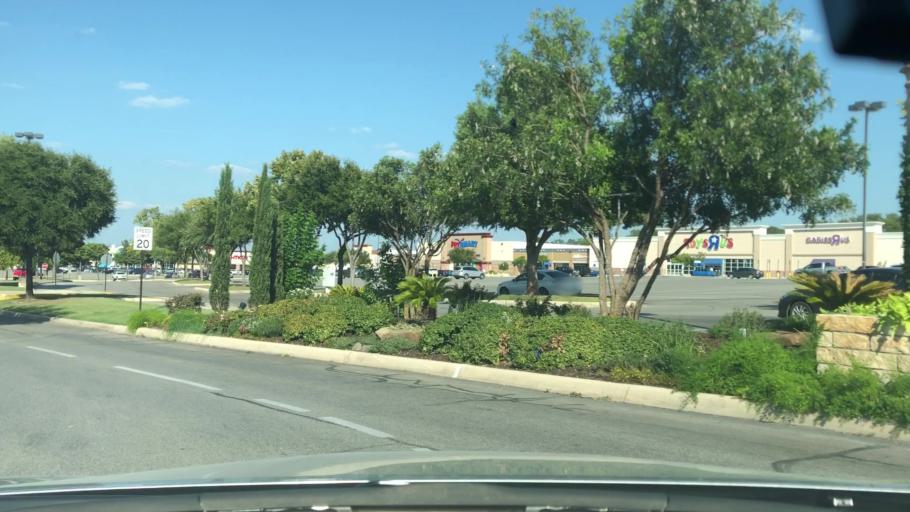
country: US
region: Texas
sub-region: Bexar County
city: Live Oak
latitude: 29.5709
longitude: -98.3264
